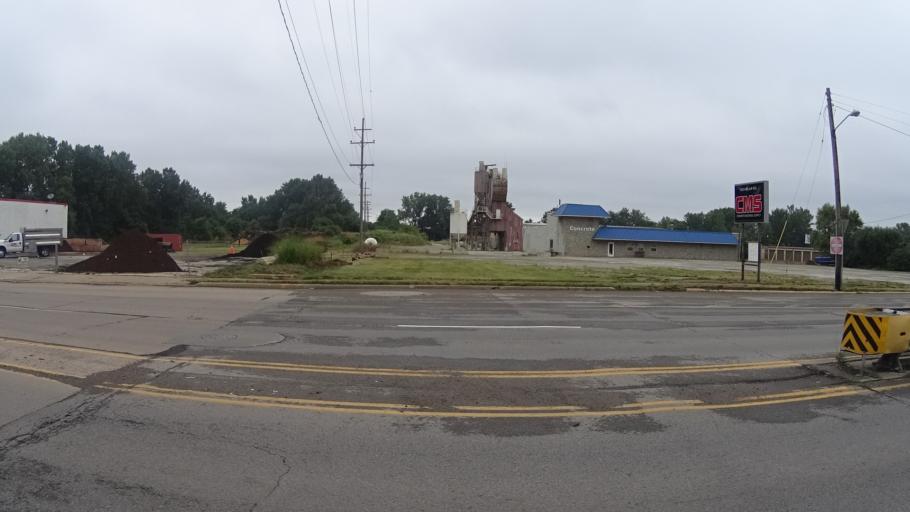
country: US
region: Ohio
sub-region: Erie County
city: Sandusky
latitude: 41.4404
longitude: -82.6959
